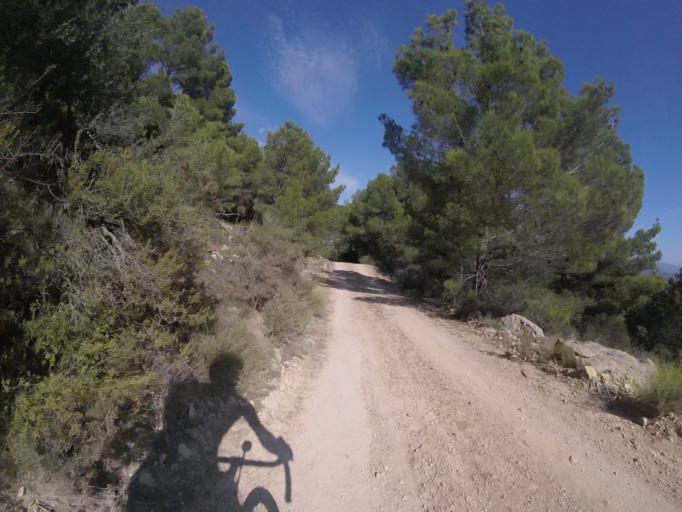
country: ES
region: Valencia
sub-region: Provincia de Castello
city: Sierra-Engarceran
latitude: 40.2714
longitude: 0.0095
